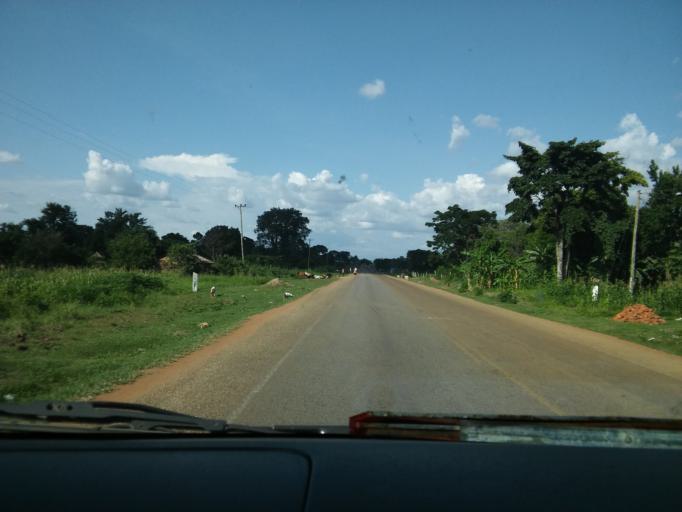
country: UG
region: Eastern Region
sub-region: Kibuku District
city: Kibuku
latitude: 1.0032
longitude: 33.7674
